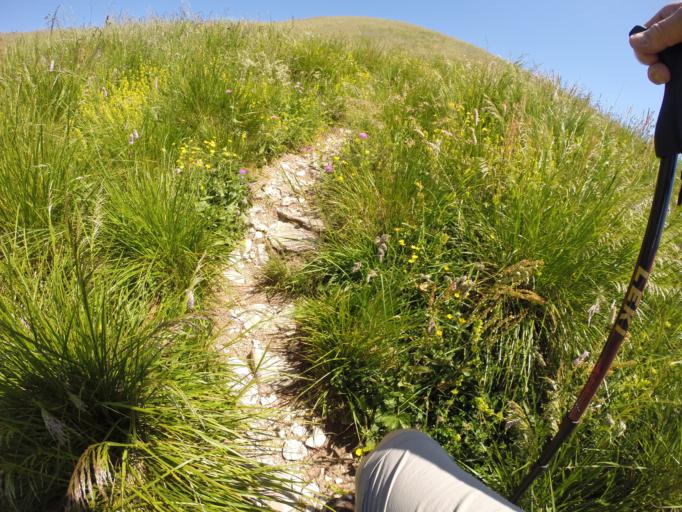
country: IT
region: Veneto
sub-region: Provincia di Treviso
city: Crespano del Grappa
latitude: 45.8998
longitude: 11.8177
